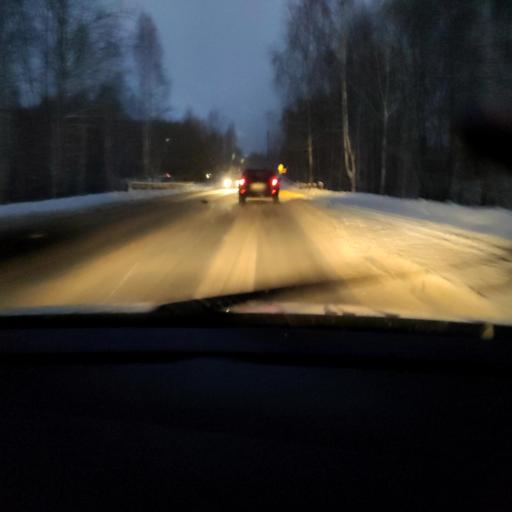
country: RU
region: Tatarstan
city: Aysha
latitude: 55.8701
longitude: 48.5798
